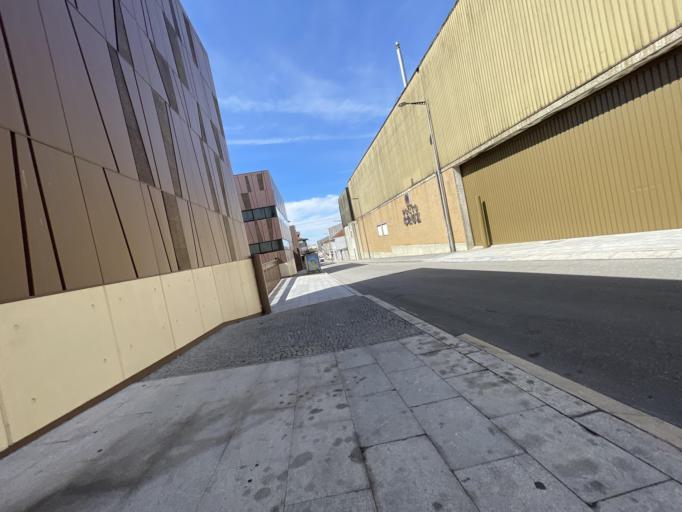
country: PT
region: Porto
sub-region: Vila Nova de Gaia
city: Vila Nova de Gaia
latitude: 41.1258
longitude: -8.6188
